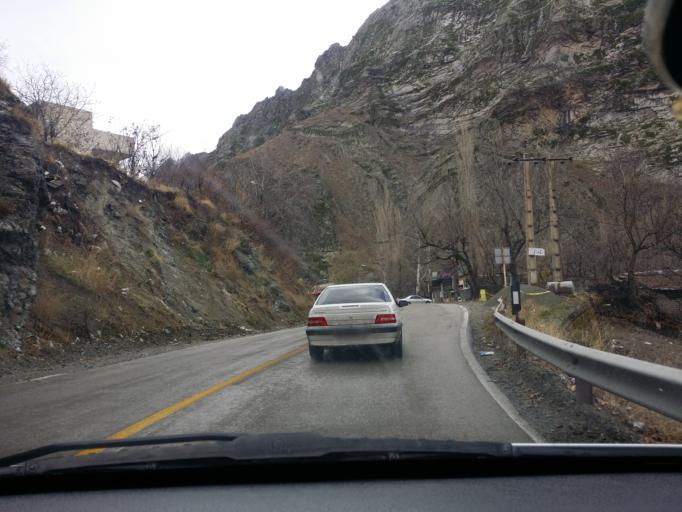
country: IR
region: Tehran
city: Tajrish
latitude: 36.0235
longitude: 51.2597
